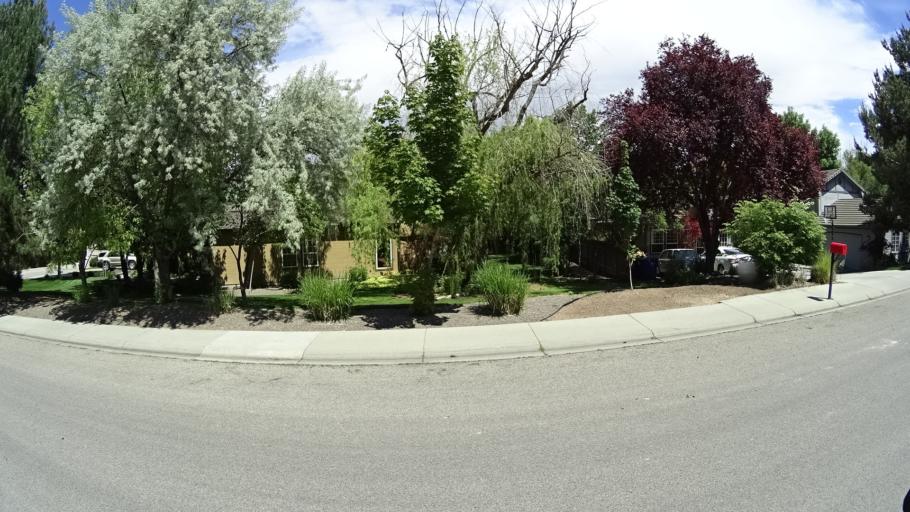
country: US
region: Idaho
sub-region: Ada County
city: Meridian
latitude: 43.5708
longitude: -116.3253
